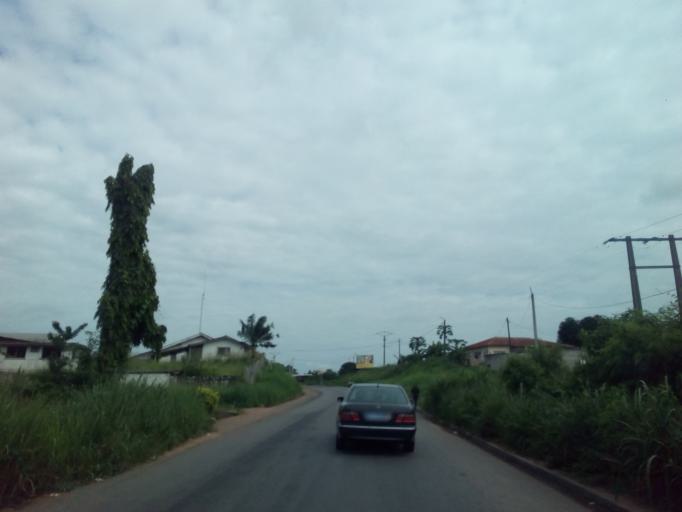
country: CI
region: Lagunes
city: Tiassale
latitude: 5.8929
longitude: -4.8177
